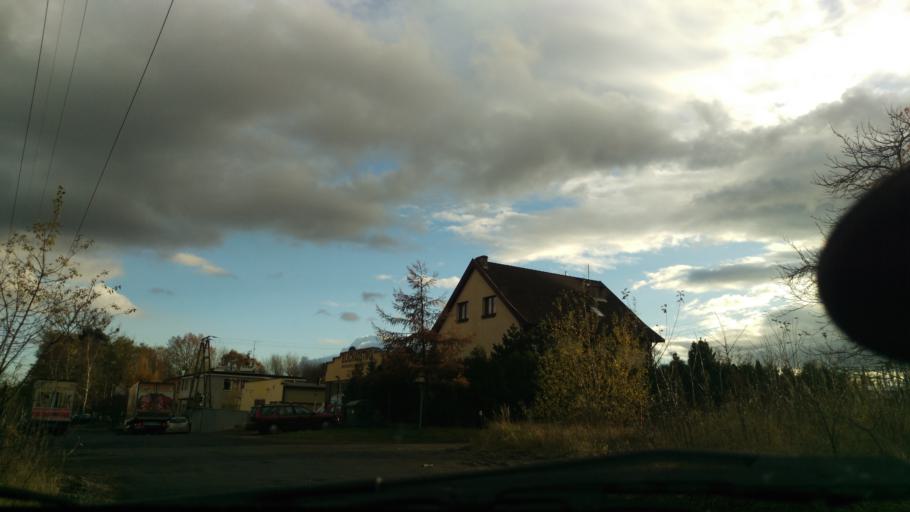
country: PL
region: West Pomeranian Voivodeship
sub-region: Szczecin
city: Szczecin
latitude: 53.3718
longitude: 14.6776
